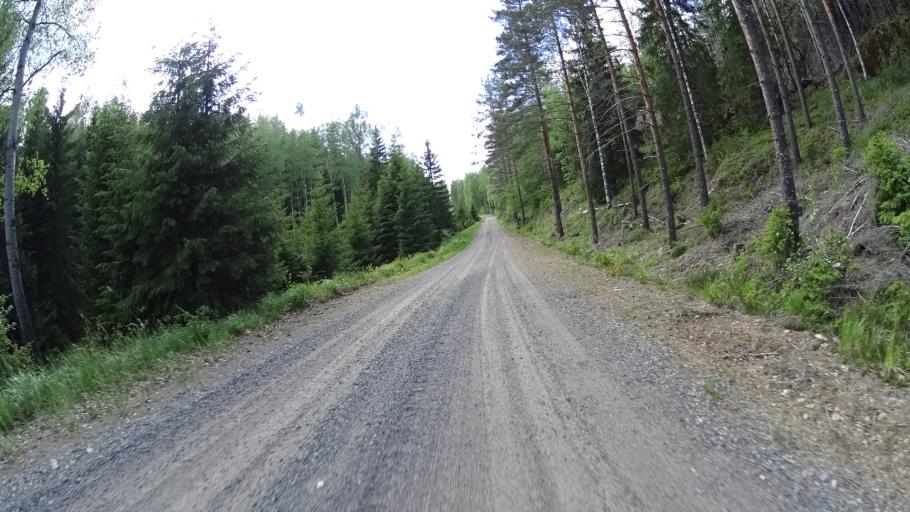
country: FI
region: Varsinais-Suomi
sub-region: Salo
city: Kisko
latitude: 60.1796
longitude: 23.5128
